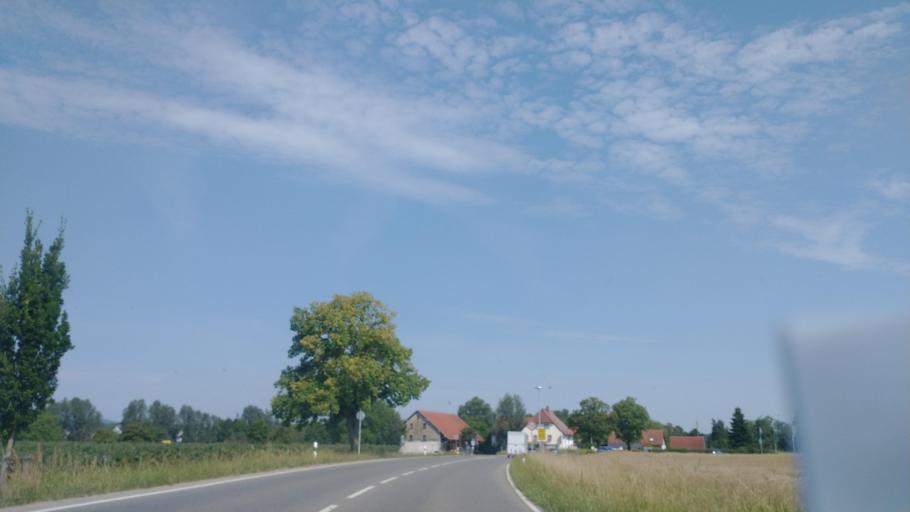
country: DE
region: Baden-Wuerttemberg
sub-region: Tuebingen Region
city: Meckenbeuren
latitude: 47.6721
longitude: 9.5383
